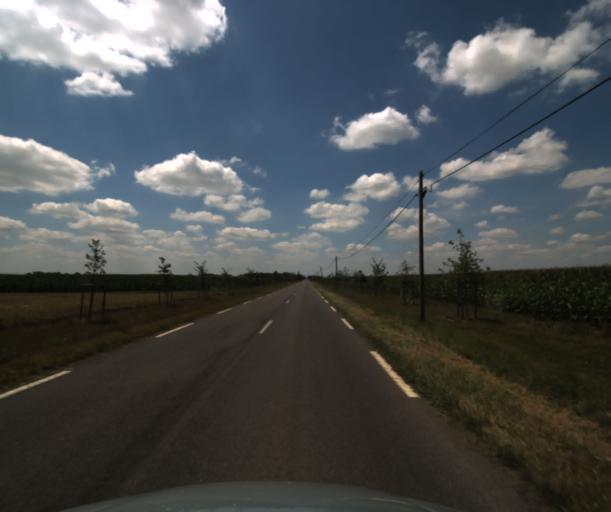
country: FR
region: Midi-Pyrenees
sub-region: Departement de la Haute-Garonne
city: Lherm
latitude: 43.4563
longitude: 1.2015
